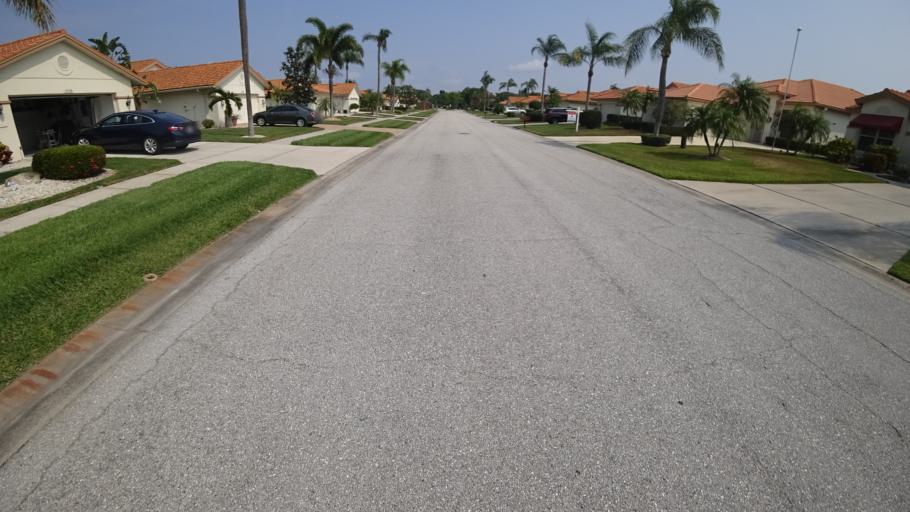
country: US
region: Florida
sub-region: Manatee County
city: Samoset
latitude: 27.4568
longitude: -82.5071
